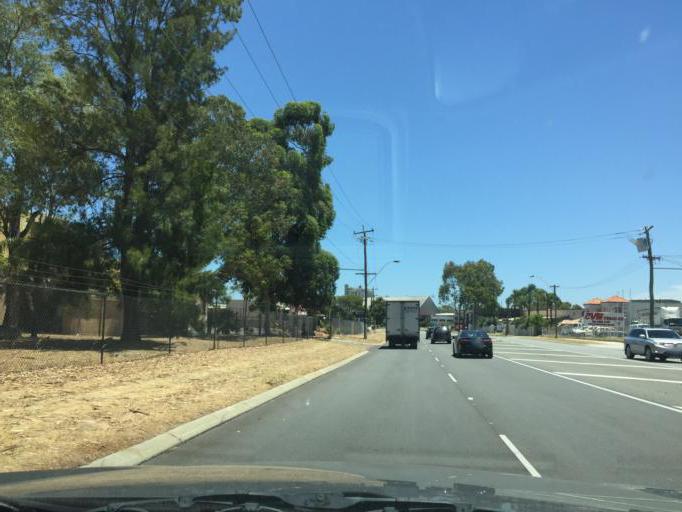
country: AU
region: Western Australia
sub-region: Canning
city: Canning Vale
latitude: -32.0597
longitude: 115.9208
